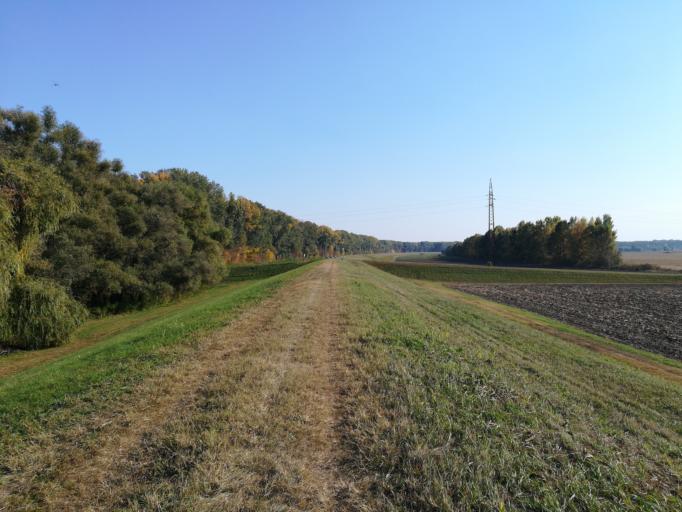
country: HU
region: Bacs-Kiskun
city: Tiszakecske
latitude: 46.9356
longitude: 20.1435
